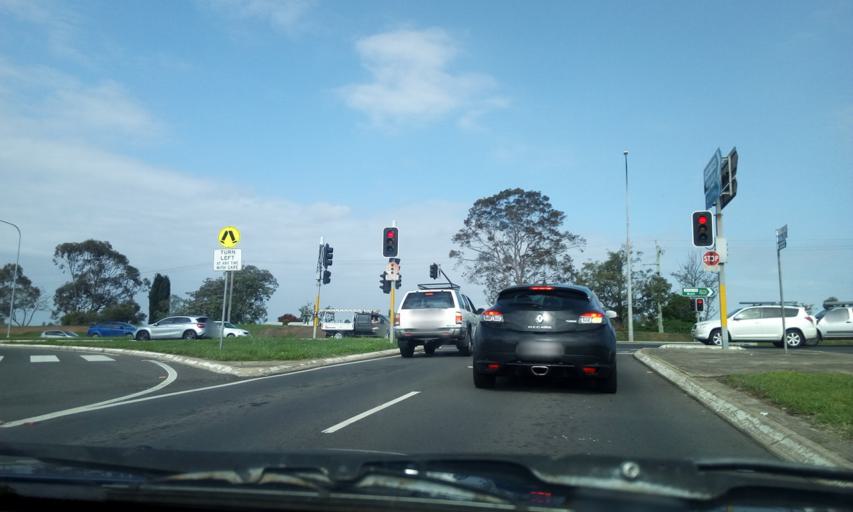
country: AU
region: New South Wales
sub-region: Campbelltown Municipality
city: Campbelltown
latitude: -34.0811
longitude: 150.8075
